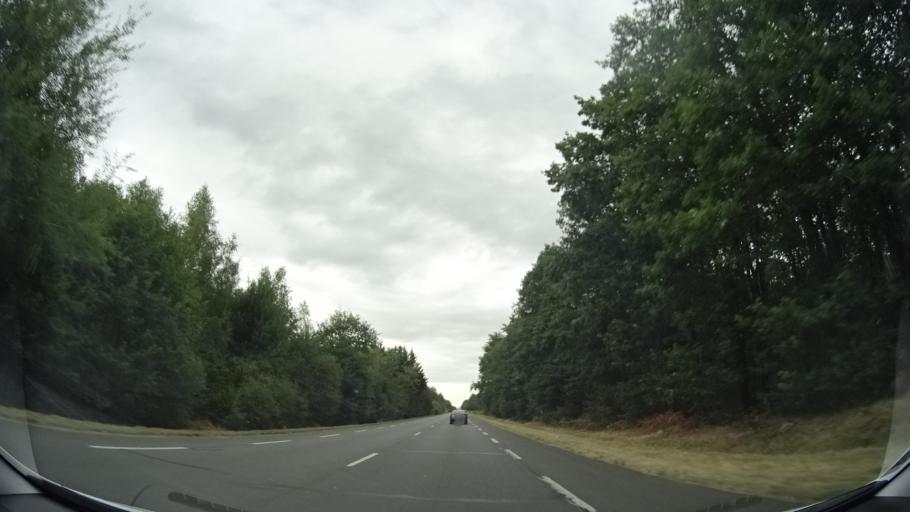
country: FR
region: Centre
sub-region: Departement du Loiret
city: Vitry-aux-Loges
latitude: 47.9307
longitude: 2.3392
